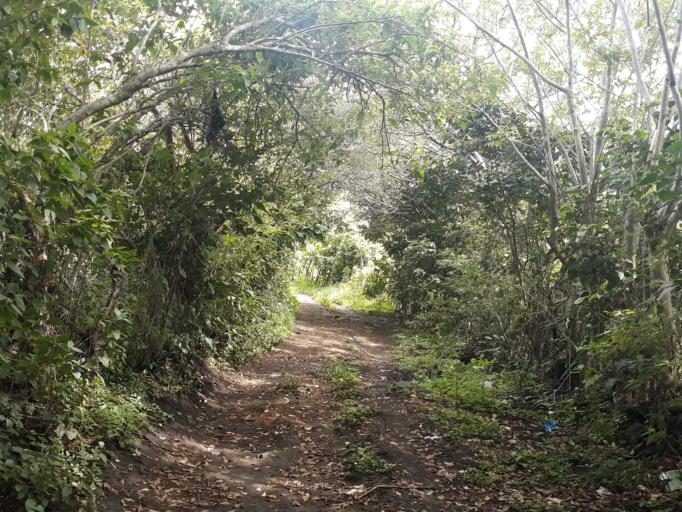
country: GT
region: Escuintla
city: San Vicente Pacaya
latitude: 14.3685
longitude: -90.5566
